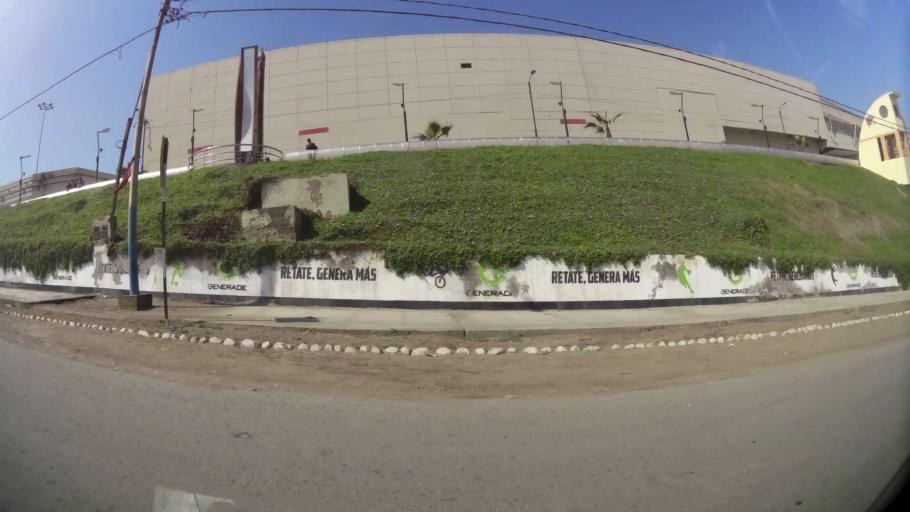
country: PE
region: Lima
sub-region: Huaura
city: Huacho
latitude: -11.1092
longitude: -77.6142
